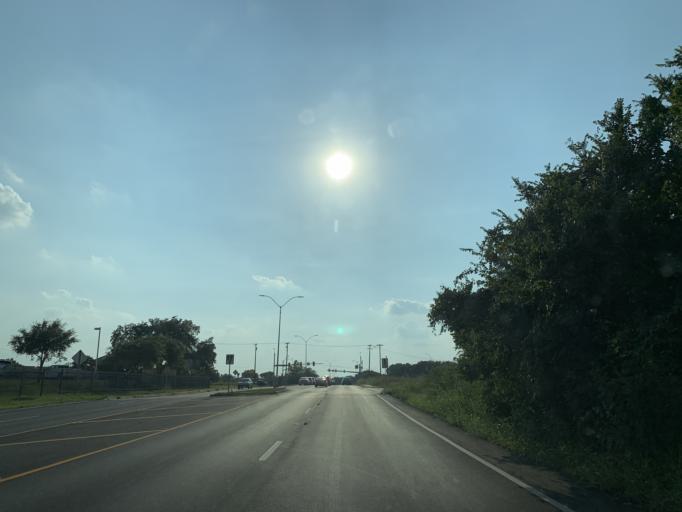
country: US
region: Texas
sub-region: Tarrant County
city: Hurst
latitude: 32.8023
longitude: -97.1815
